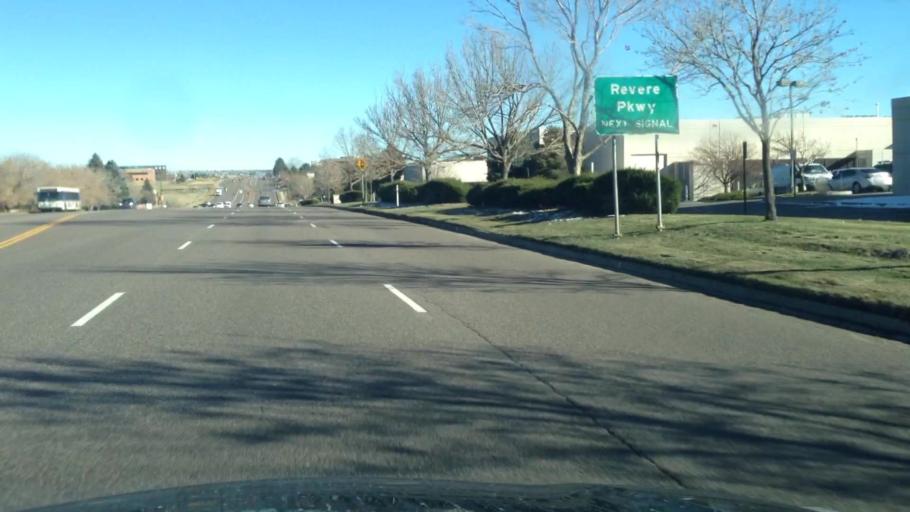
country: US
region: Colorado
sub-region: Arapahoe County
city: Dove Valley
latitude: 39.5949
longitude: -104.8442
